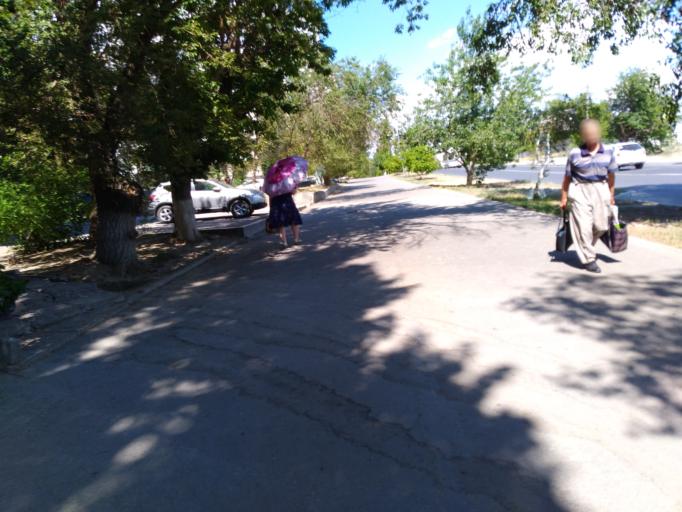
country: RU
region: Volgograd
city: Volgograd
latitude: 48.7177
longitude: 44.5177
